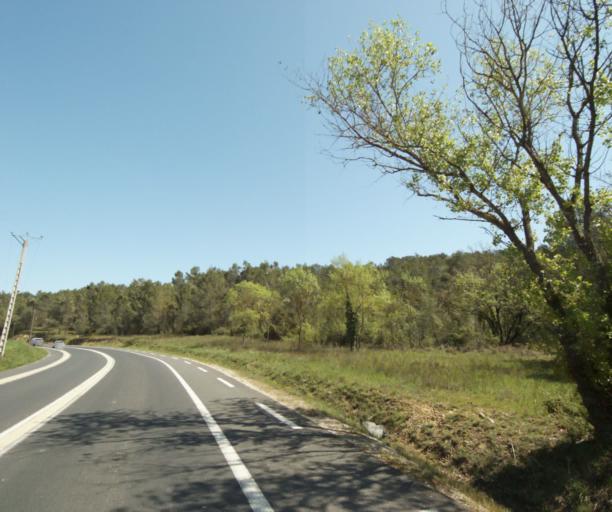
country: FR
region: Languedoc-Roussillon
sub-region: Departement de l'Herault
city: Montferrier-sur-Lez
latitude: 43.6680
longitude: 3.8679
